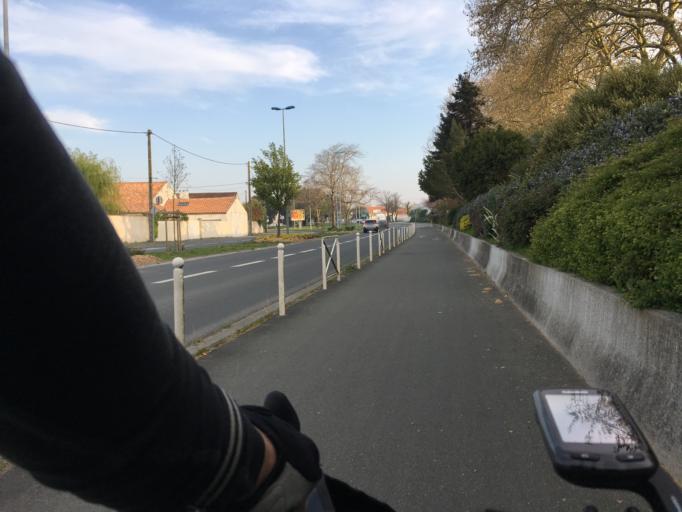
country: FR
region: Poitou-Charentes
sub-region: Departement de la Charente-Maritime
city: La Rochelle
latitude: 46.1756
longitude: -1.1505
